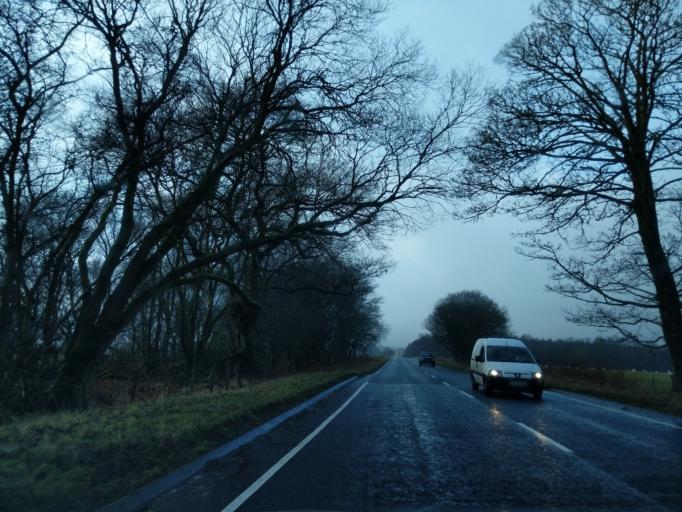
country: GB
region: Scotland
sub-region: Perth and Kinross
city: Kinross
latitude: 56.2020
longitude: -3.4913
